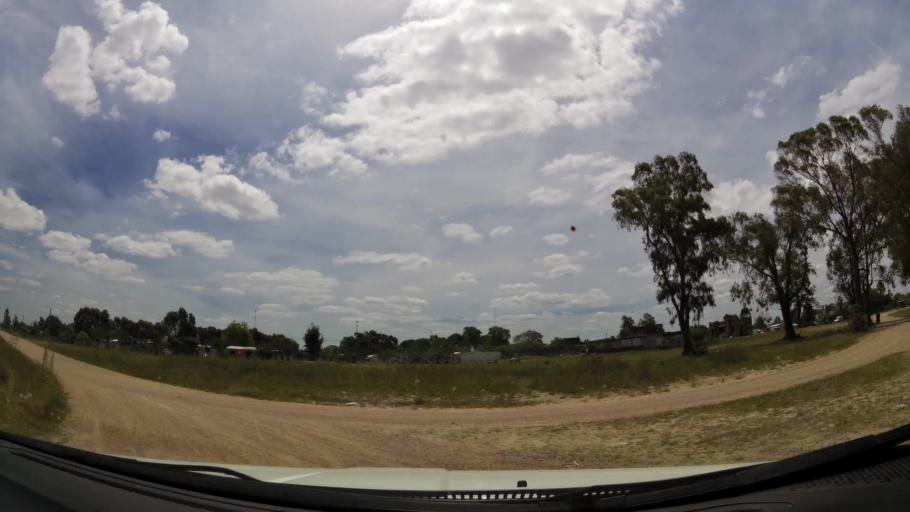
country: UY
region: San Jose
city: Delta del Tigre
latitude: -34.7619
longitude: -56.4046
